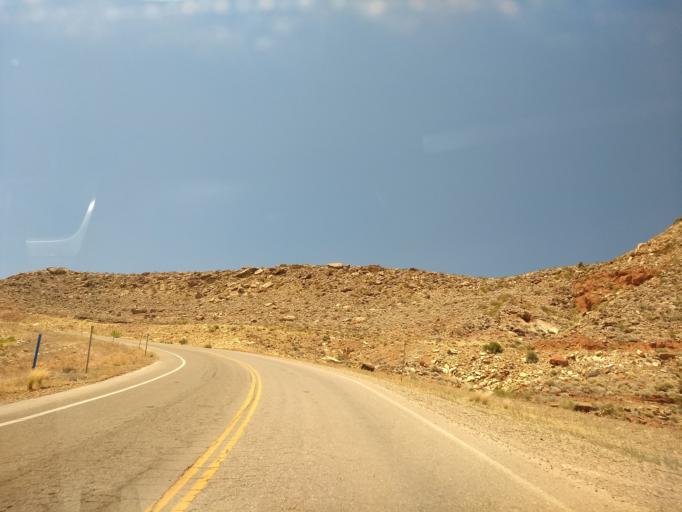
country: US
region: Utah
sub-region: Washington County
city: Washington
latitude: 37.1361
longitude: -113.4573
